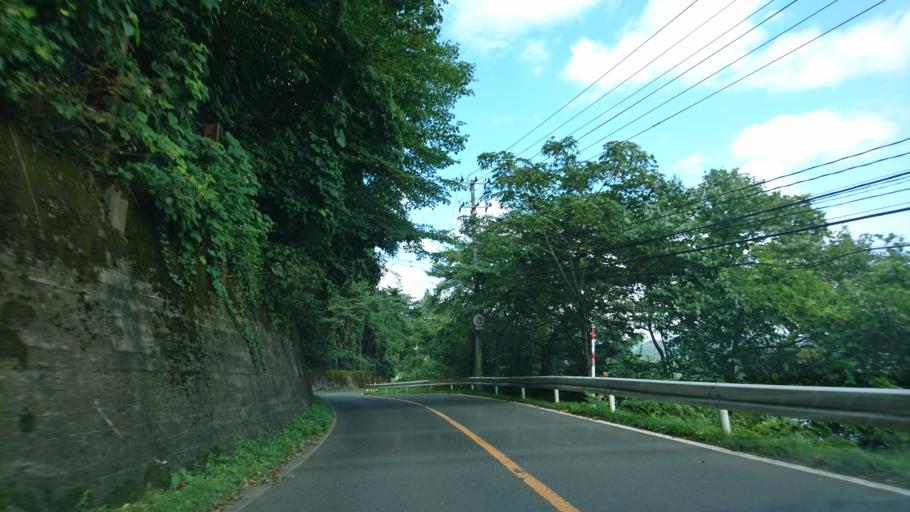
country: JP
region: Miyagi
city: Furukawa
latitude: 38.7841
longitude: 140.8481
